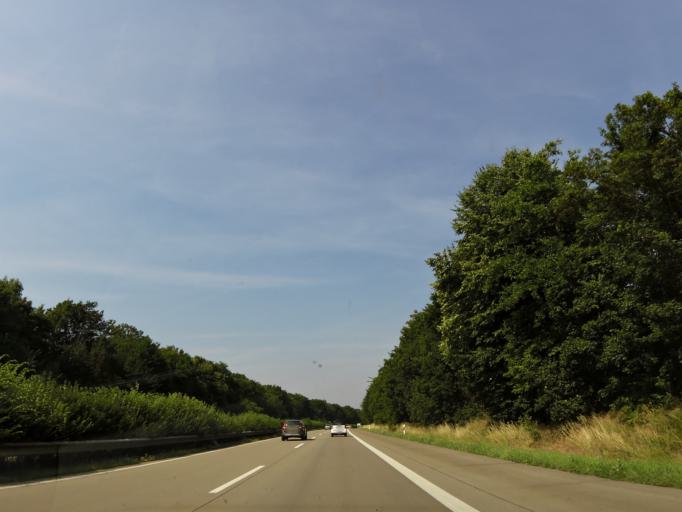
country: DE
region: Rheinland-Pfalz
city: Bassenheim
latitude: 50.3649
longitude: 7.4451
